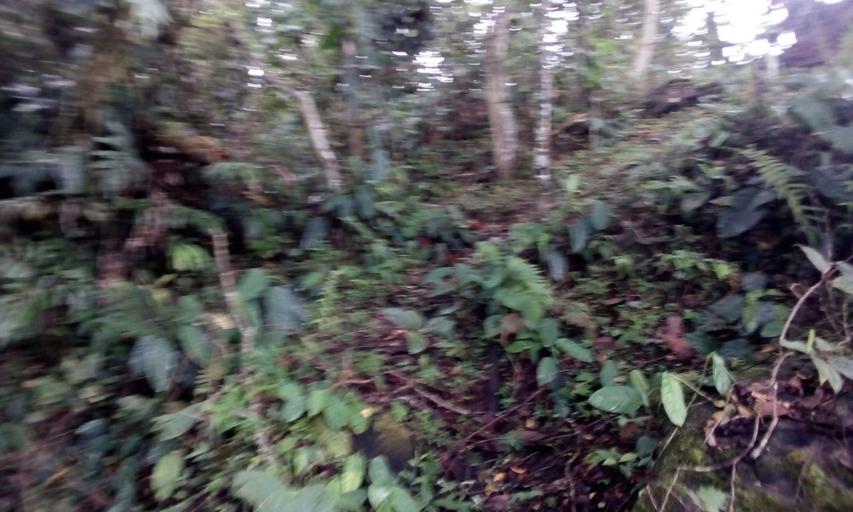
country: CO
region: Boyaca
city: Santana
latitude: 6.0046
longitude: -73.4940
